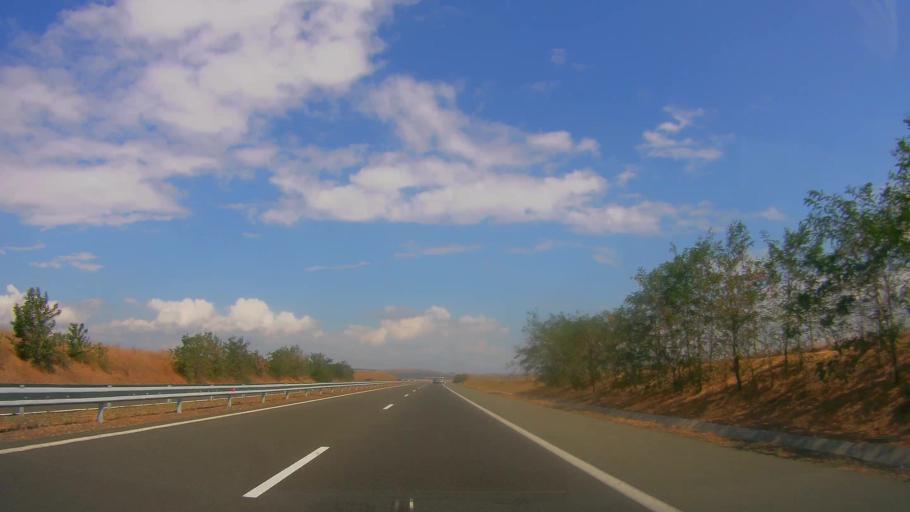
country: BG
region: Burgas
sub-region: Obshtina Karnobat
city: Karnobat
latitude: 42.5862
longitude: 26.9416
